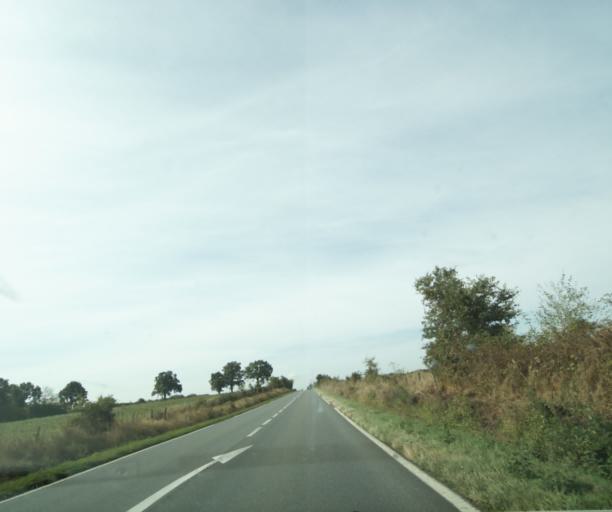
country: FR
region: Auvergne
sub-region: Departement de l'Allier
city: Saint-Francois
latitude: 46.3770
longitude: 3.8697
